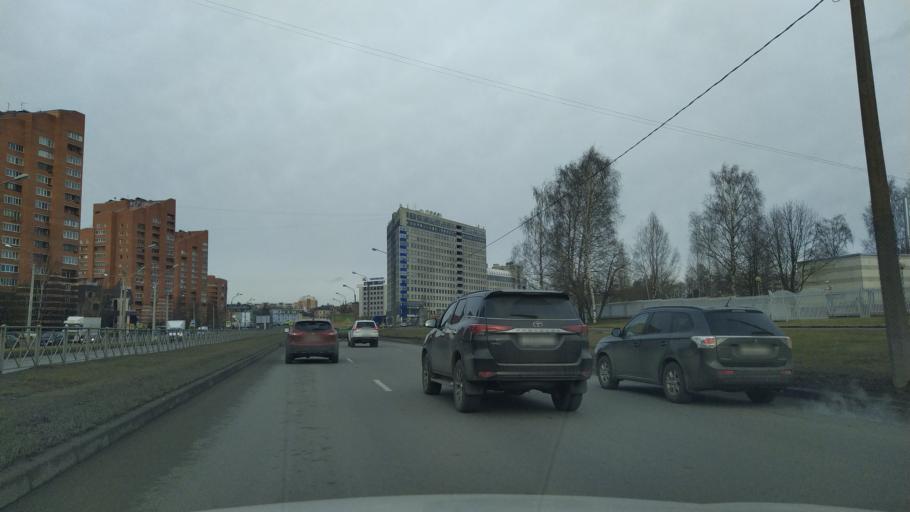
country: RU
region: St.-Petersburg
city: Kolomyagi
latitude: 60.0106
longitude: 30.2954
